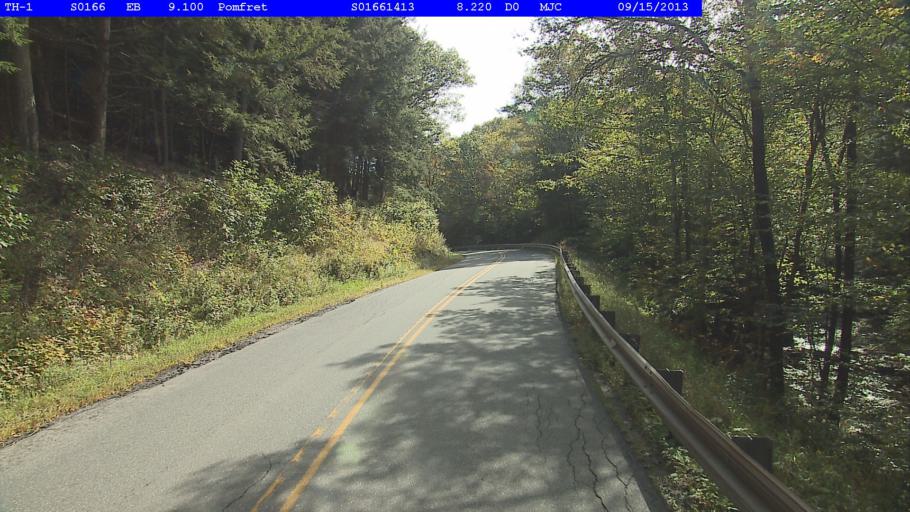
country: US
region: Vermont
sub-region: Windsor County
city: Woodstock
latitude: 43.7238
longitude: -72.4592
